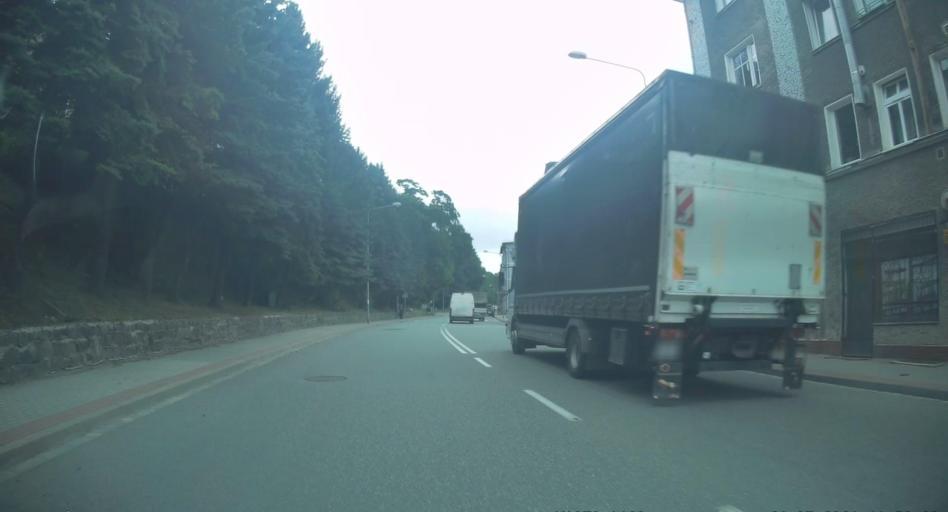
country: PL
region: Lower Silesian Voivodeship
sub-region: Powiat walbrzyski
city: Walbrzych
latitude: 50.7710
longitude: 16.3059
